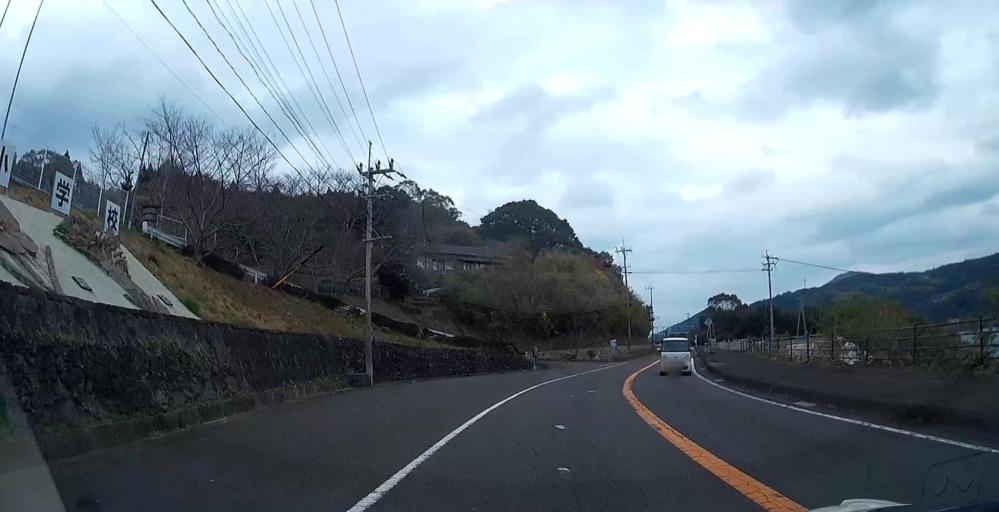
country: JP
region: Kagoshima
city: Akune
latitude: 32.0990
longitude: 130.1664
